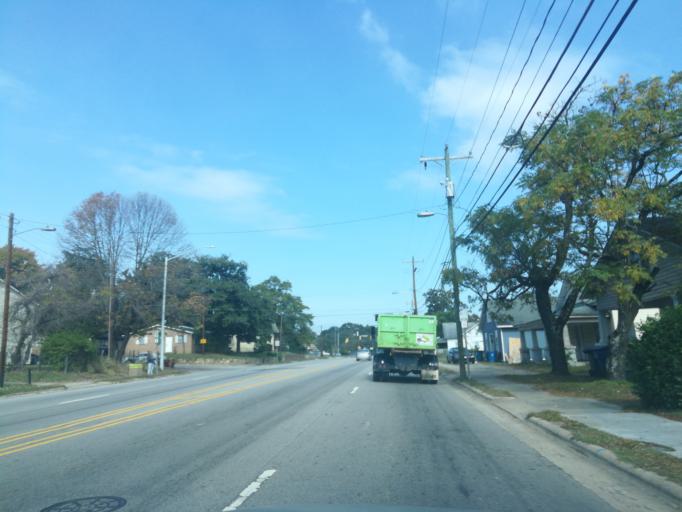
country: US
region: North Carolina
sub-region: Durham County
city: Durham
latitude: 35.9780
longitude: -78.8924
